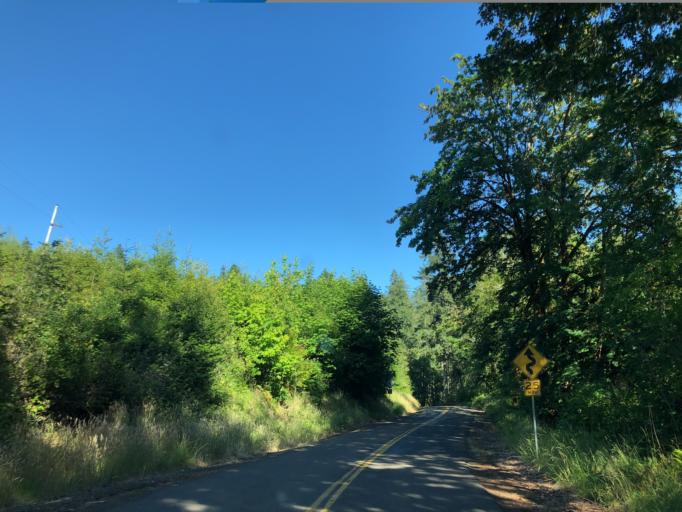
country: US
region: Oregon
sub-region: Linn County
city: Sweet Home
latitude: 44.4654
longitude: -122.6855
